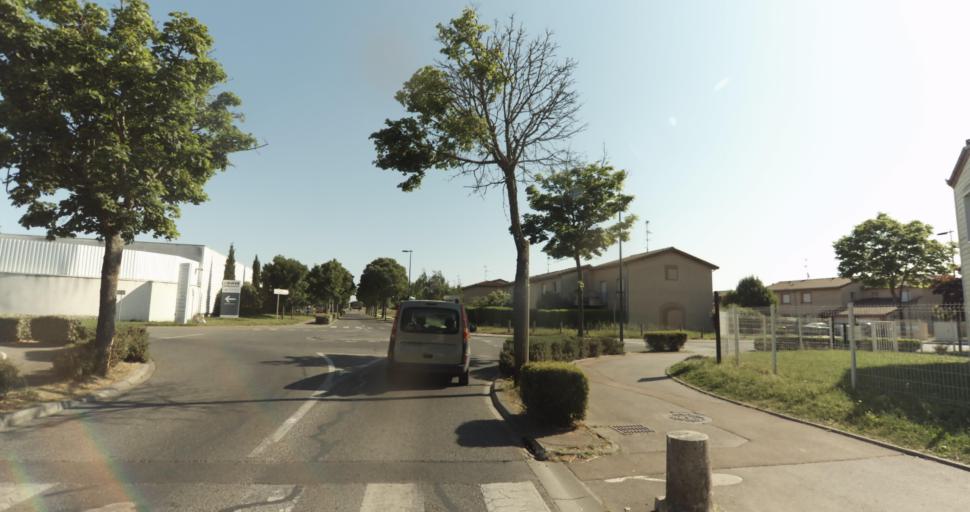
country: FR
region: Midi-Pyrenees
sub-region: Departement de la Haute-Garonne
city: Plaisance-du-Touch
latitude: 43.5682
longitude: 1.3090
